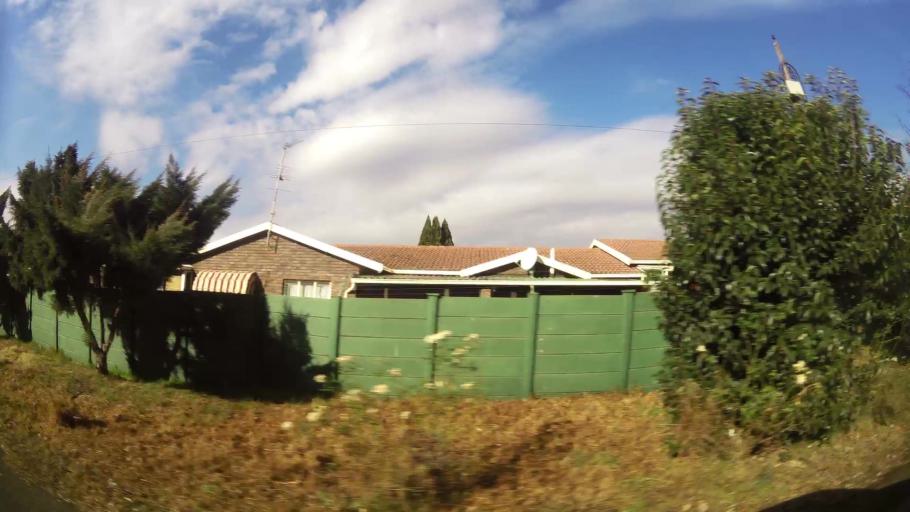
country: ZA
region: Gauteng
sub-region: Sedibeng District Municipality
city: Meyerton
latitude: -26.5479
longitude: 28.0624
